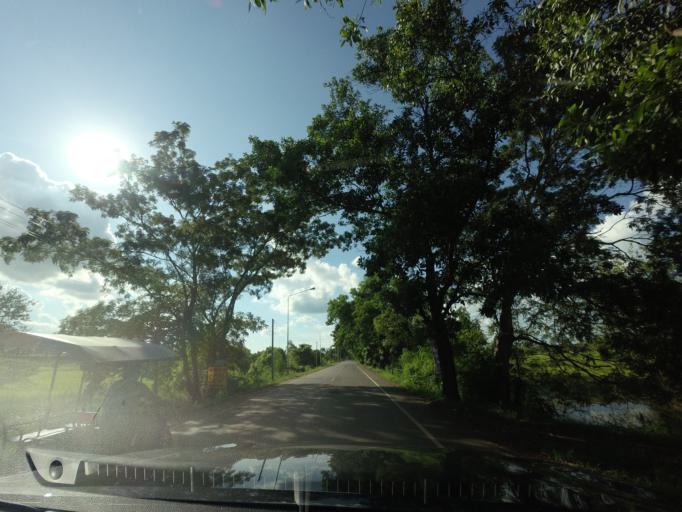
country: TH
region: Changwat Udon Thani
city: Ban Dung
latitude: 17.7398
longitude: 103.3452
